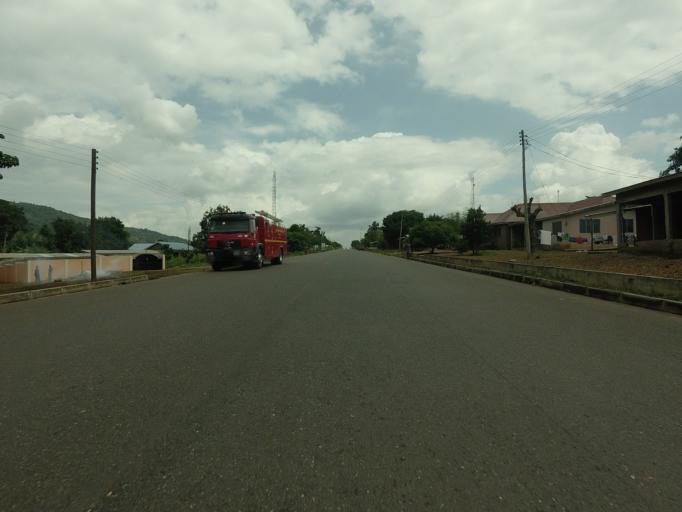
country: GH
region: Volta
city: Ho
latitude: 6.5345
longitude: 0.2304
